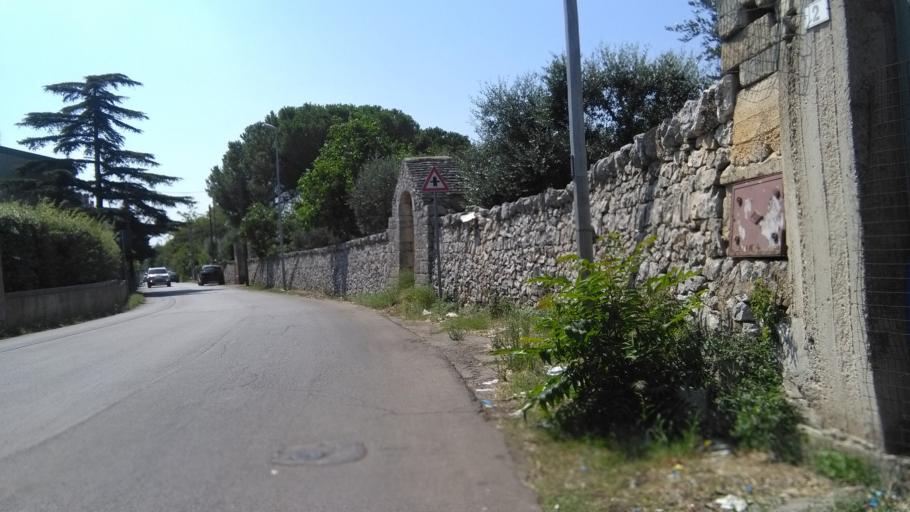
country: IT
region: Apulia
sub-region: Provincia di Bari
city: Putignano
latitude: 40.8459
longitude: 17.1283
